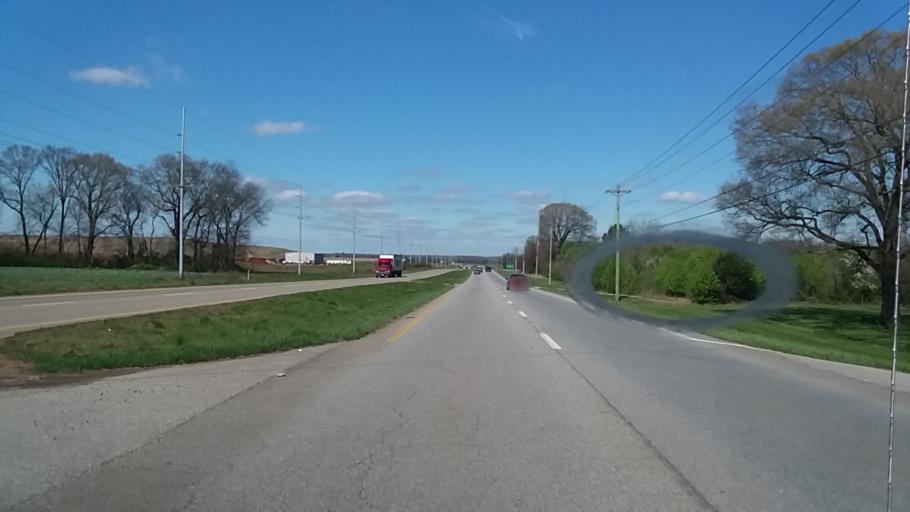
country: US
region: Alabama
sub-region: Morgan County
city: Trinity
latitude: 34.6278
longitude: -87.0902
